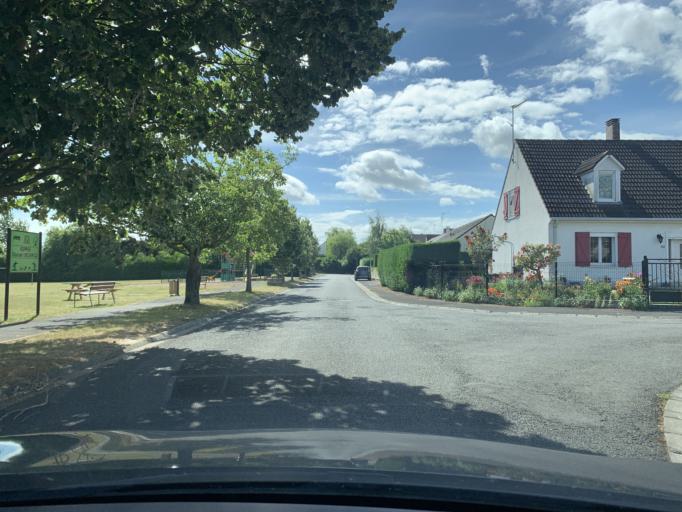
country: FR
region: Nord-Pas-de-Calais
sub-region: Departement du Nord
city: Marcoing
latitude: 50.1380
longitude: 3.1774
